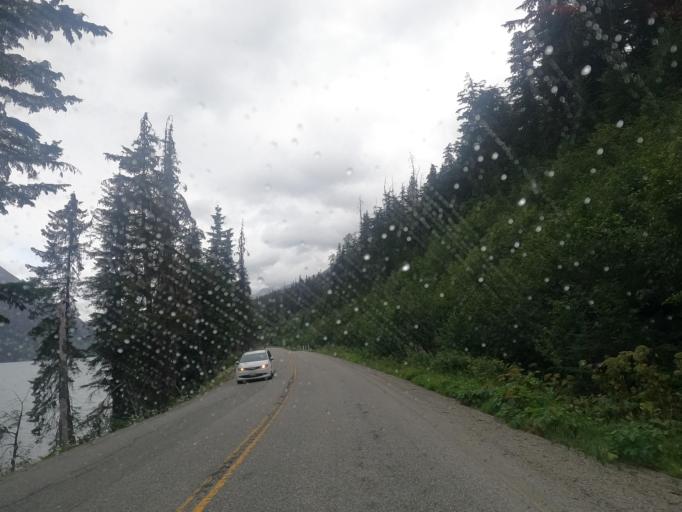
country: CA
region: British Columbia
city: Lillooet
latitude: 50.3981
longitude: -122.3176
